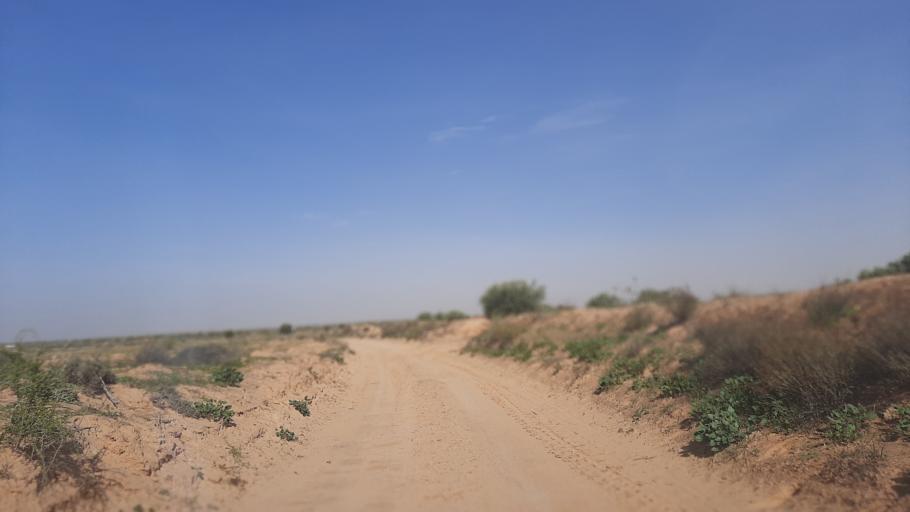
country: TN
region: Madanin
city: Zarzis
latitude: 33.4422
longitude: 10.8083
